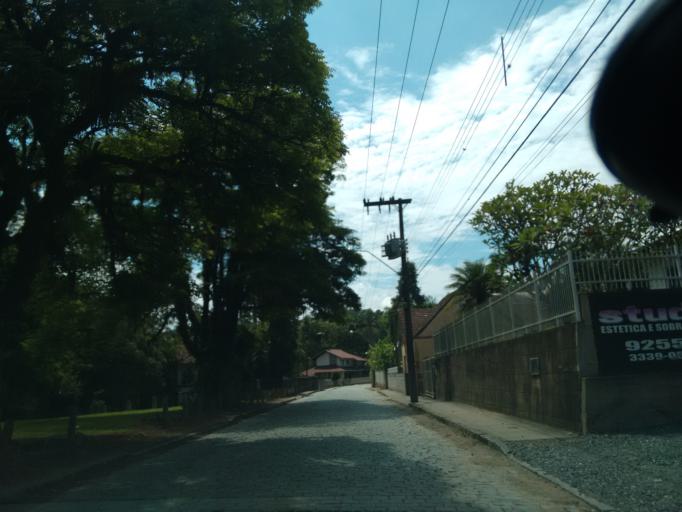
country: BR
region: Santa Catarina
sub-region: Indaial
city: Indaial
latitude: -26.8530
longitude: -49.1534
